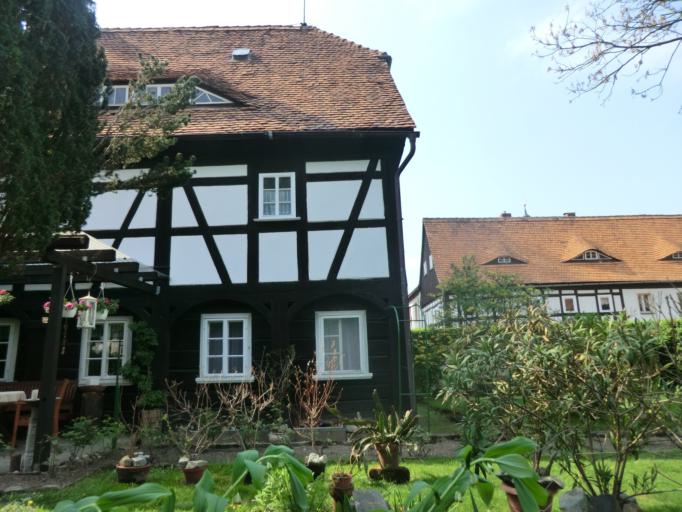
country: DE
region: Saxony
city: Grossschonau
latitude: 50.8975
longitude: 14.6640
